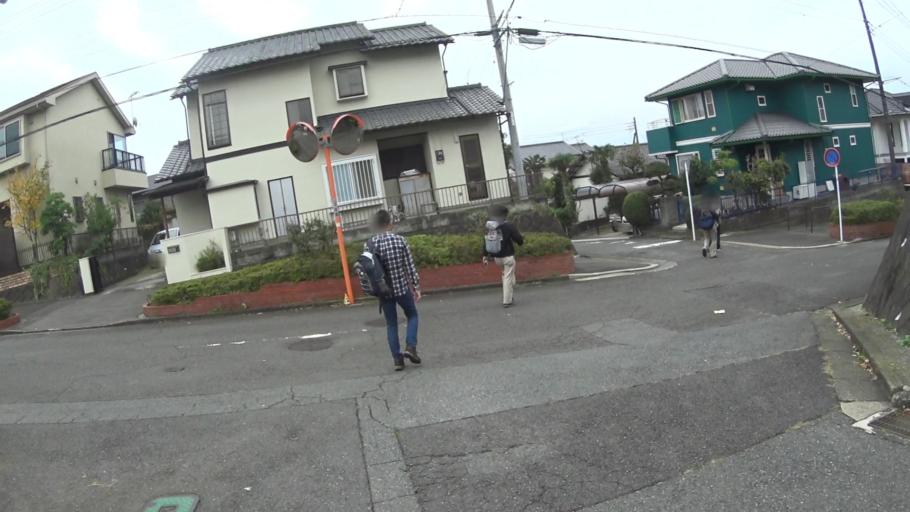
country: JP
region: Kanagawa
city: Hadano
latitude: 35.3850
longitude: 139.2204
